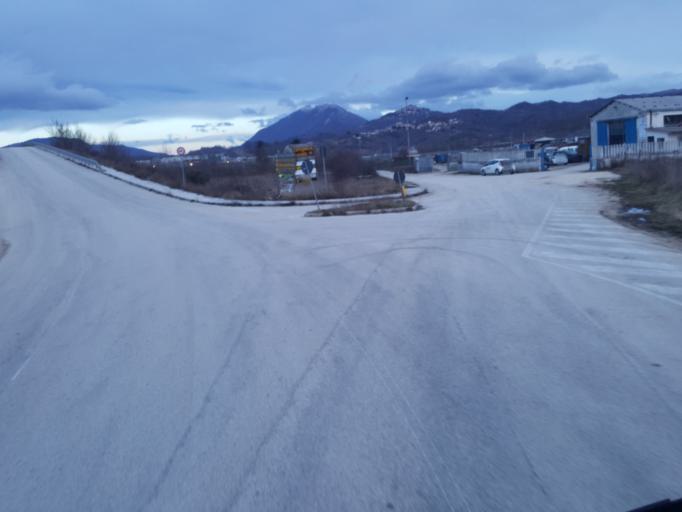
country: IT
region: Abruzzo
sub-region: Provincia dell' Aquila
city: Carsoli
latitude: 42.0814
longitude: 13.0566
